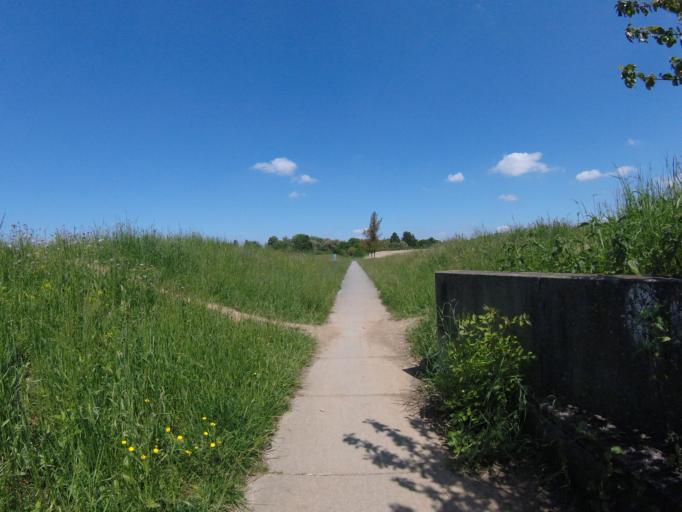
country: DE
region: Bavaria
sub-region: Upper Bavaria
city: Unterhaching
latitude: 48.0692
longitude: 11.6252
